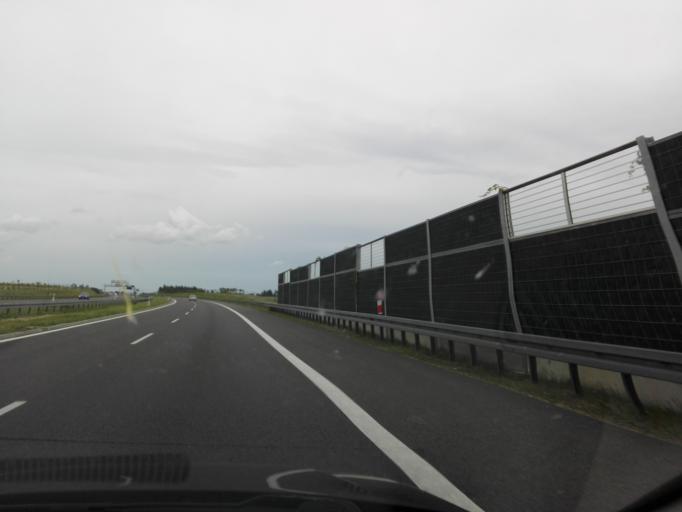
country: PL
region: Lublin Voivodeship
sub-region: Powiat lubelski
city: Jastkow
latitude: 51.2928
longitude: 22.4156
